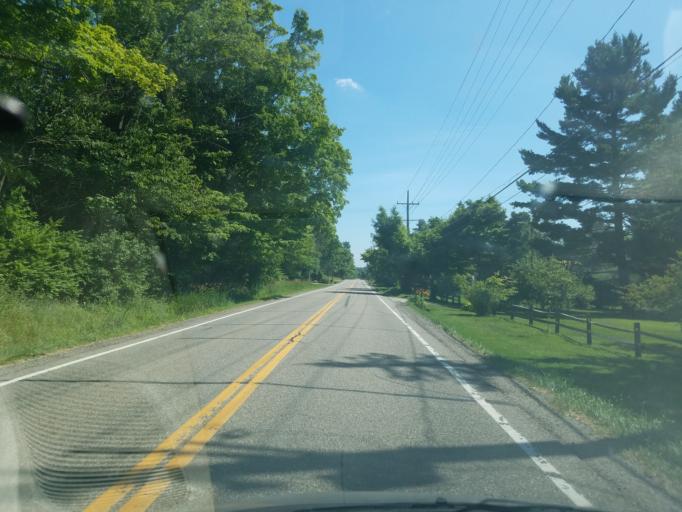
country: US
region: Ohio
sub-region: Geauga County
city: Burton
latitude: 41.5158
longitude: -81.1442
